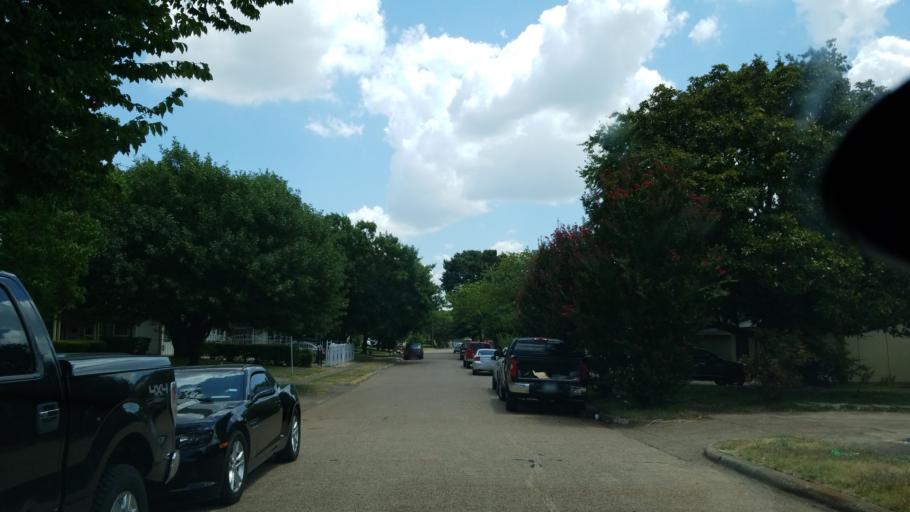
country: US
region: Texas
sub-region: Dallas County
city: Cockrell Hill
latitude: 32.7148
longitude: -96.8991
